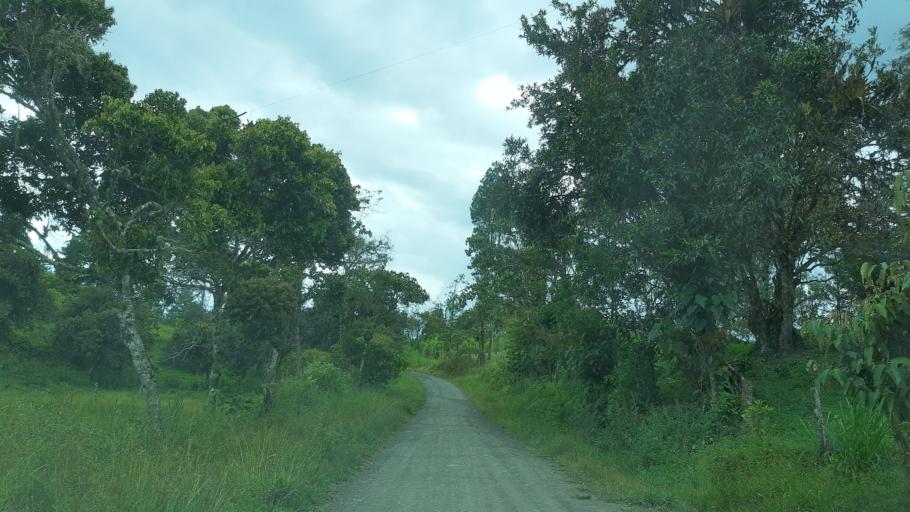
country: CO
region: Boyaca
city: Garagoa
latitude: 5.0202
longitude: -73.3311
